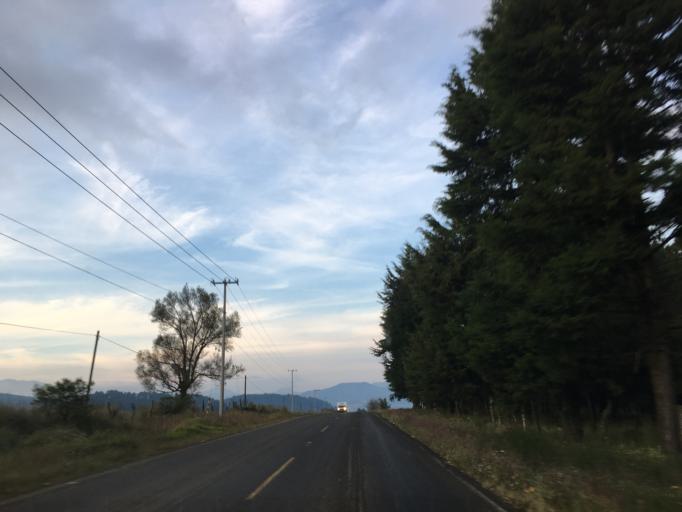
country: MX
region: Michoacan
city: Angahuan
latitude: 19.5872
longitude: -102.2369
